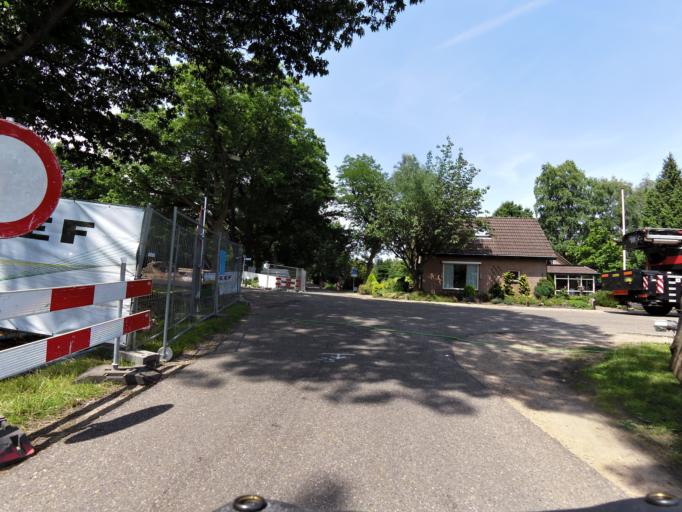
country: NL
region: Gelderland
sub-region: Gemeente Apeldoorn
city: Loenen
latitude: 52.1524
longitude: 6.0334
